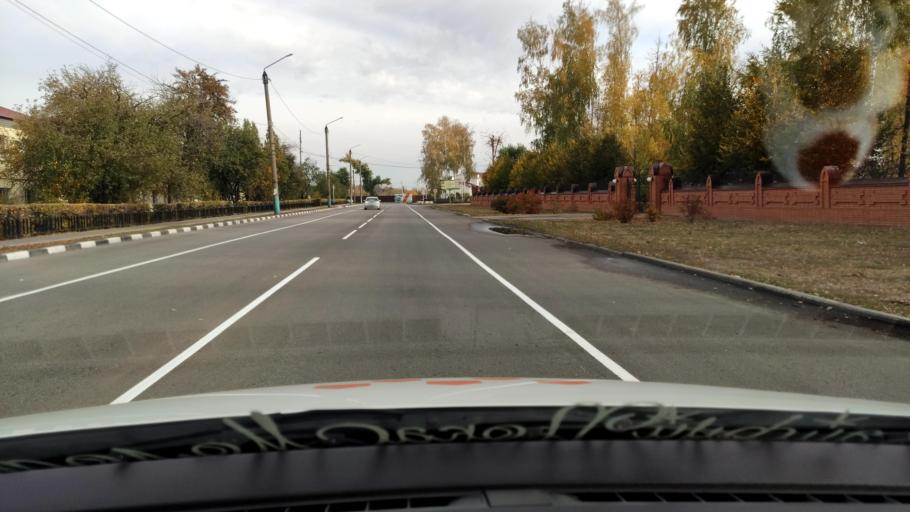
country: RU
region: Voronezj
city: Ramon'
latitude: 51.9090
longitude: 39.3361
